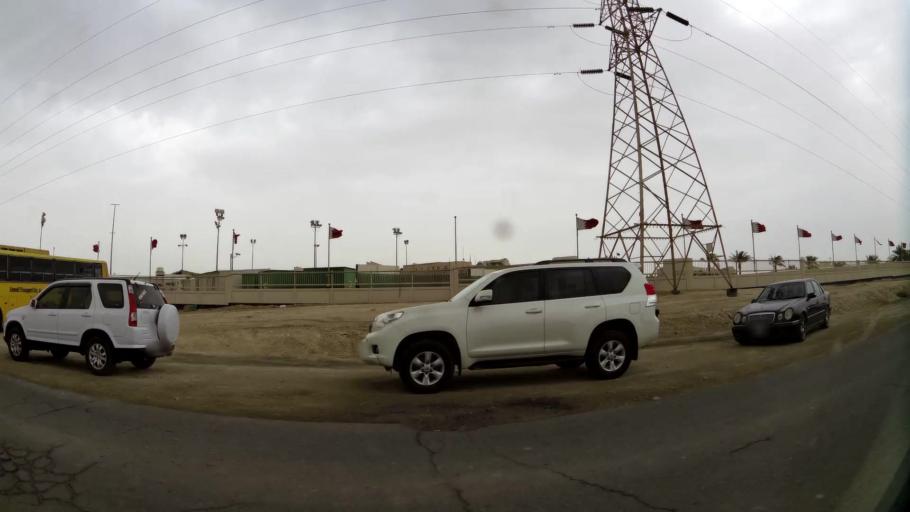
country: BH
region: Northern
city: Madinat `Isa
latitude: 26.1621
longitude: 50.5471
